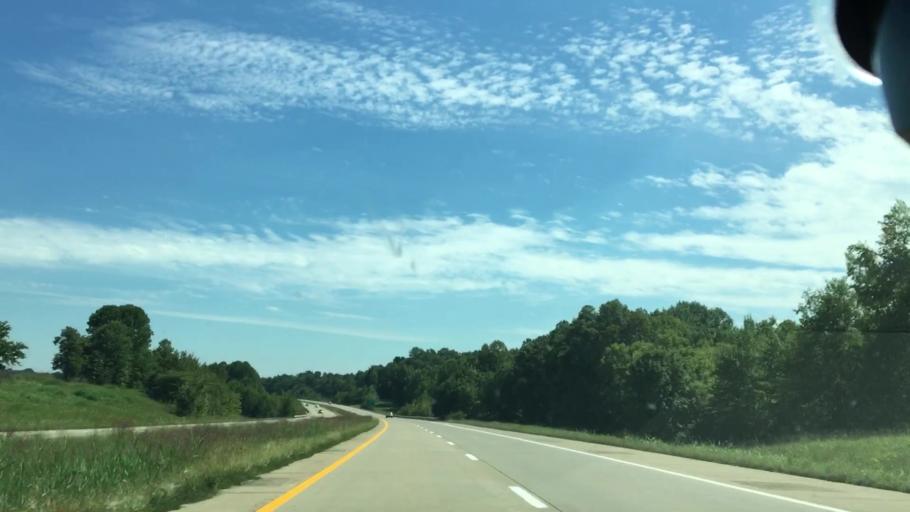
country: US
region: Indiana
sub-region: Warrick County
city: Newburgh
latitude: 37.7577
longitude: -87.4124
